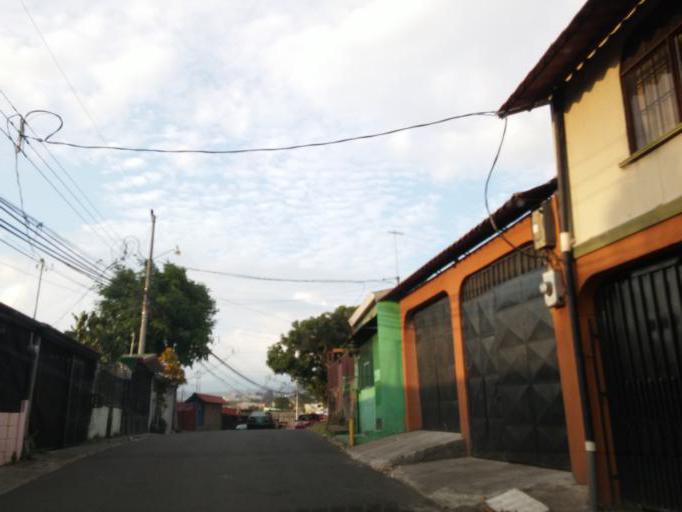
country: CR
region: Alajuela
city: Alajuela
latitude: 10.0022
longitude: -84.2210
